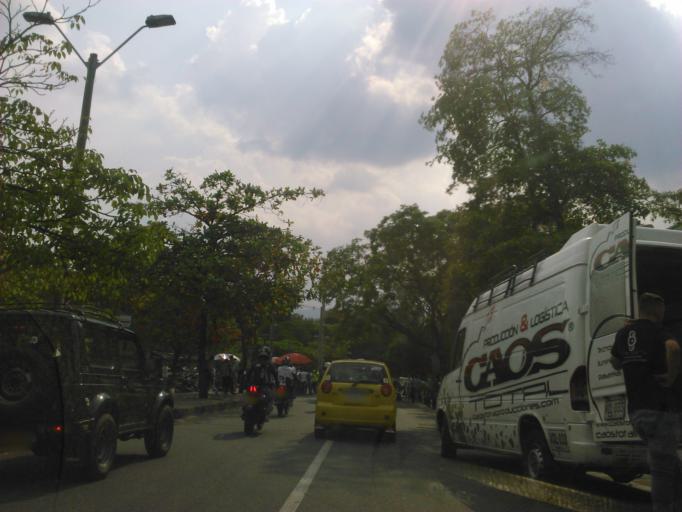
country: CO
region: Antioquia
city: Medellin
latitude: 6.2541
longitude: -75.5884
